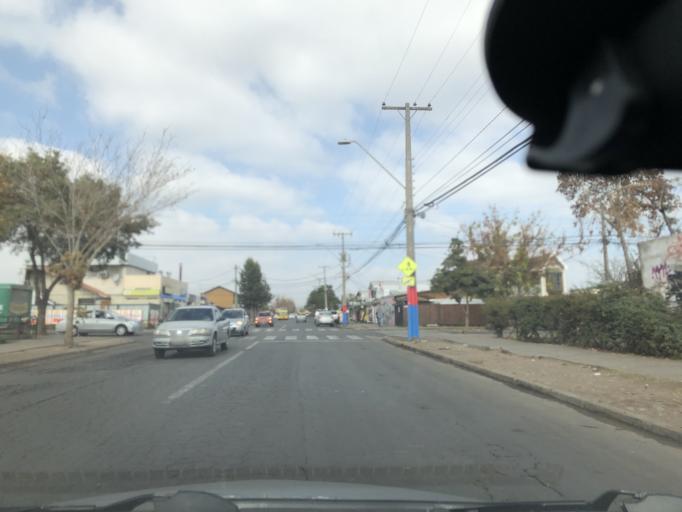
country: CL
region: Santiago Metropolitan
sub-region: Provincia de Cordillera
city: Puente Alto
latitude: -33.5825
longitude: -70.5921
